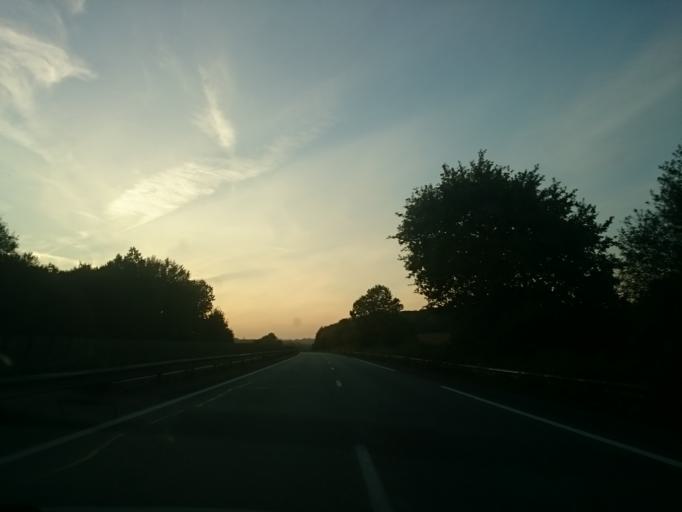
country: FR
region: Brittany
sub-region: Departement du Finistere
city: Saint-Yvi
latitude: 47.9303
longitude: -3.9023
